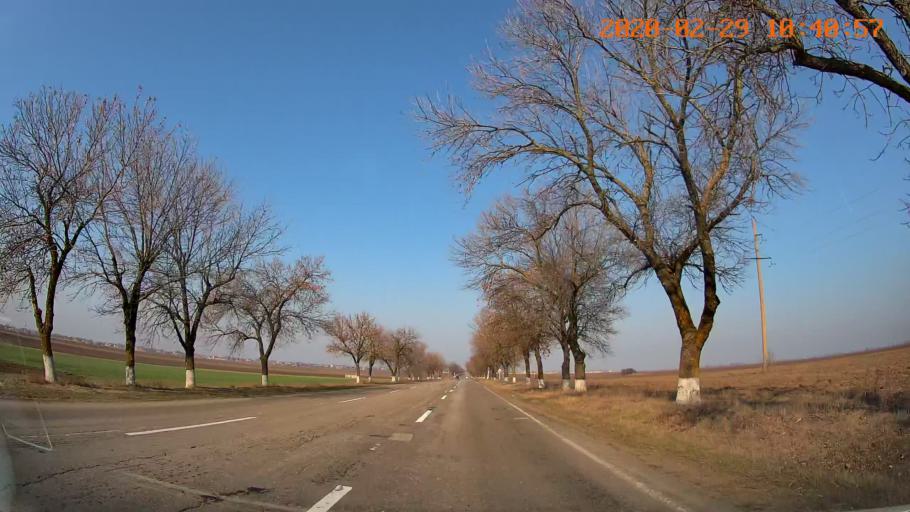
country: MD
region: Anenii Noi
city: Varnita
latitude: 47.0379
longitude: 29.4321
